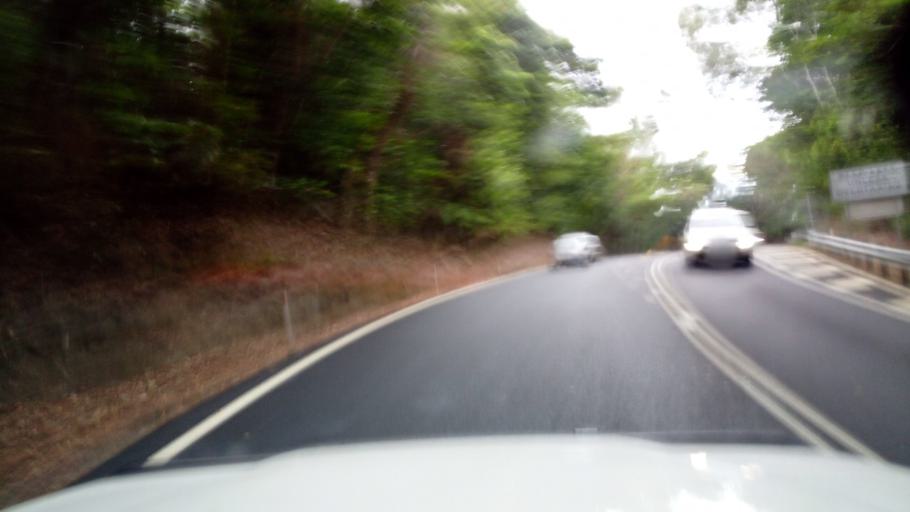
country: AU
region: Queensland
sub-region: Tablelands
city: Kuranda
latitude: -16.8306
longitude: 145.6664
